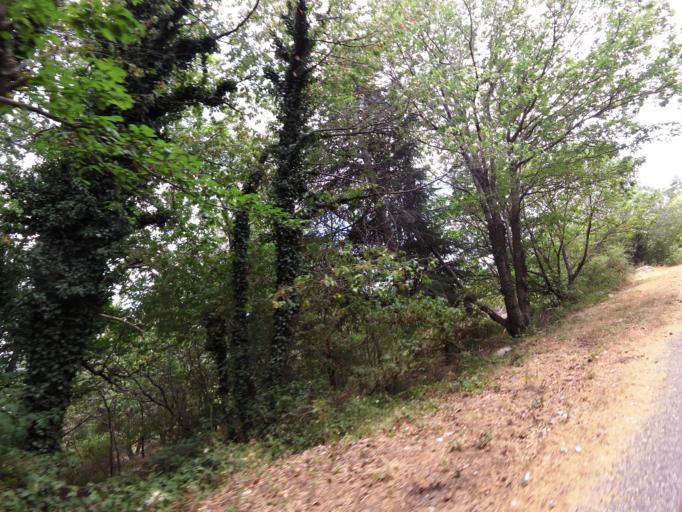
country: FR
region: Languedoc-Roussillon
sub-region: Departement du Gard
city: Le Vigan
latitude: 44.0362
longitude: 3.6069
